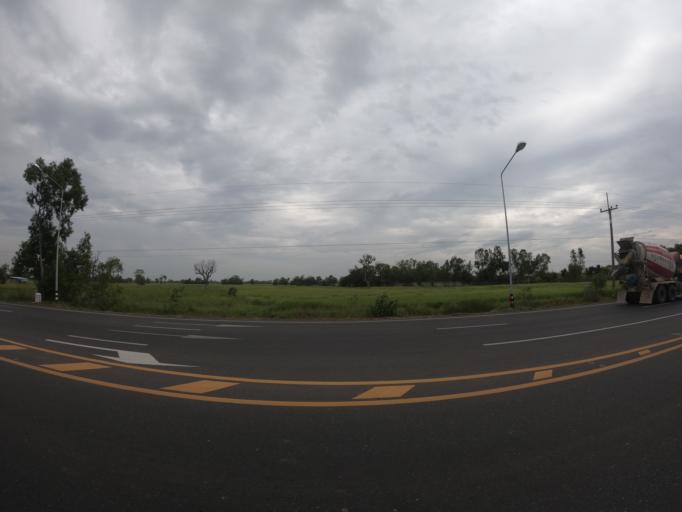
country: TH
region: Roi Et
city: Thawat Buri
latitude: 16.0894
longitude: 103.7657
